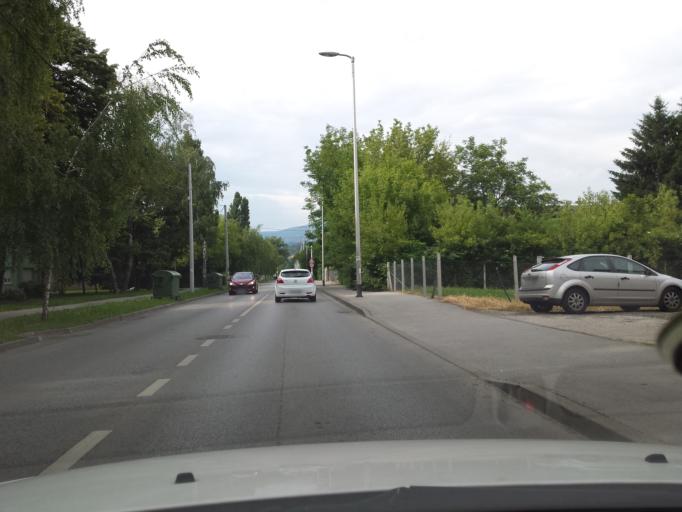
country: HR
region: Grad Zagreb
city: Jankomir
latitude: 45.8038
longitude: 15.9302
